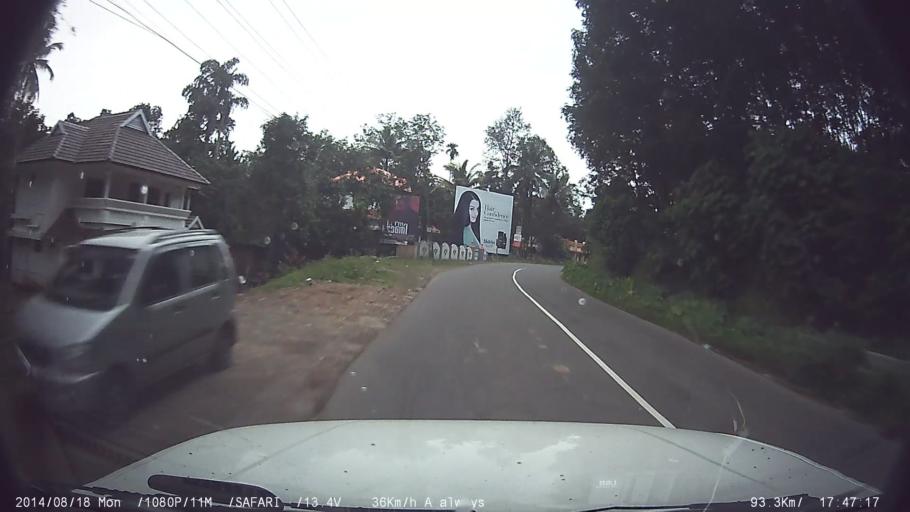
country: IN
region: Kerala
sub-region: Ernakulam
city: Muvattupuzha
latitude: 9.9601
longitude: 76.5756
